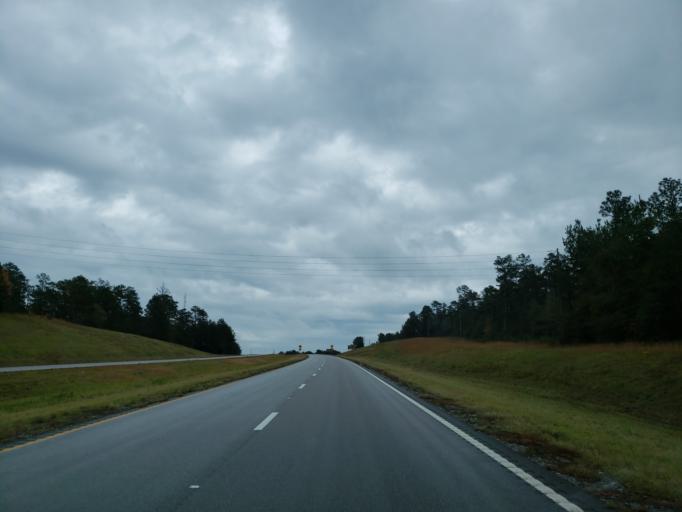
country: US
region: Mississippi
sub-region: Wayne County
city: Waynesboro
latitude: 31.6847
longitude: -88.6993
